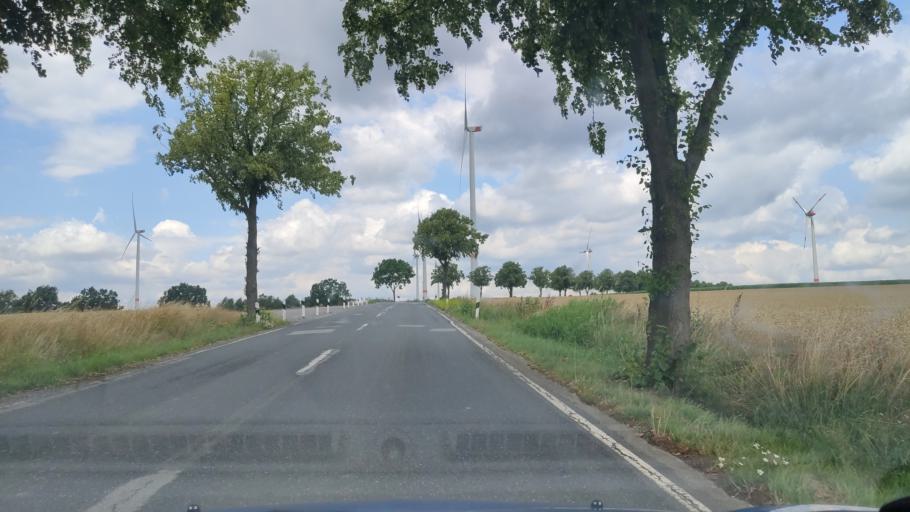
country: DE
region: Lower Saxony
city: Coppenbrugge
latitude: 52.1181
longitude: 9.5039
